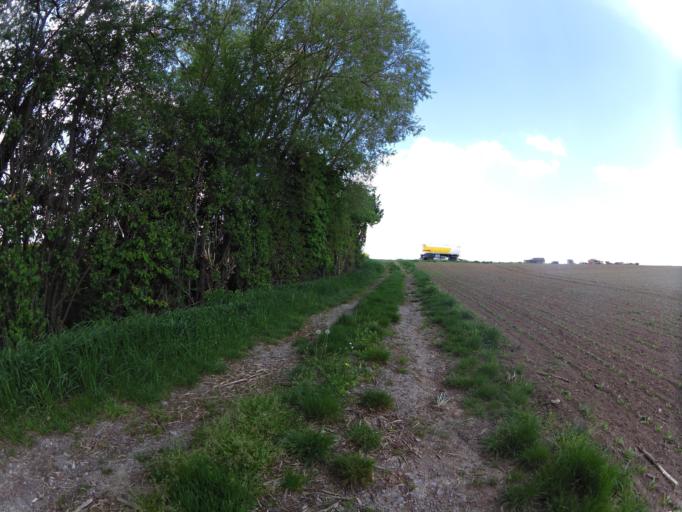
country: DE
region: Bavaria
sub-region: Regierungsbezirk Unterfranken
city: Sulzdorf
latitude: 49.6260
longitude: 9.9132
